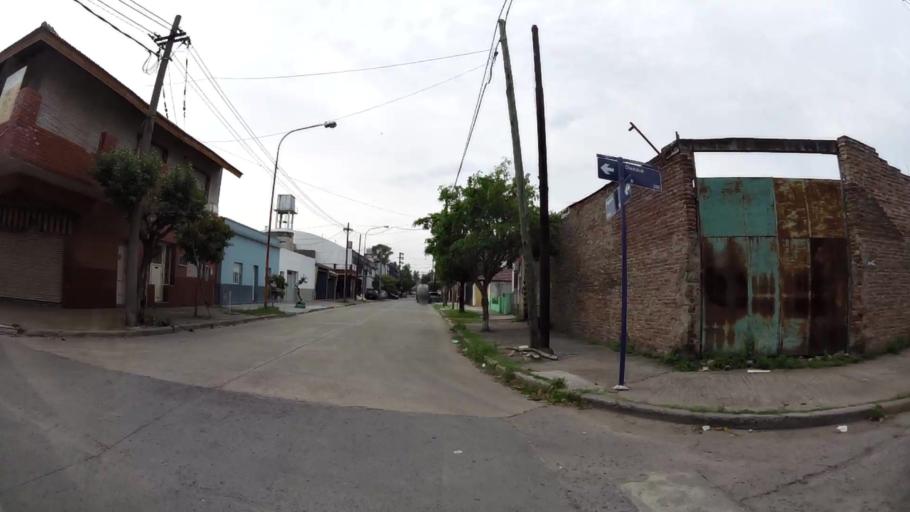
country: AR
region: Buenos Aires
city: San Justo
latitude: -34.6860
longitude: -58.5175
